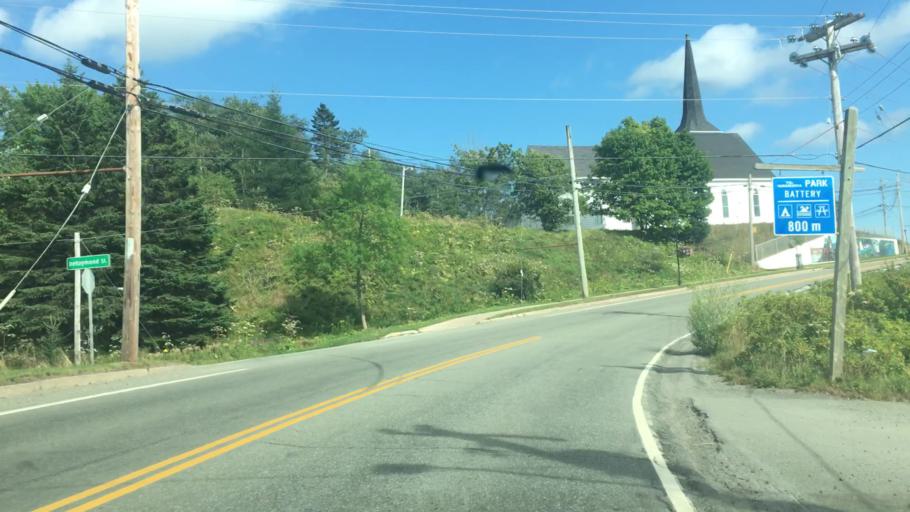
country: CA
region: Nova Scotia
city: Princeville
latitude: 45.6558
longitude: -60.8807
